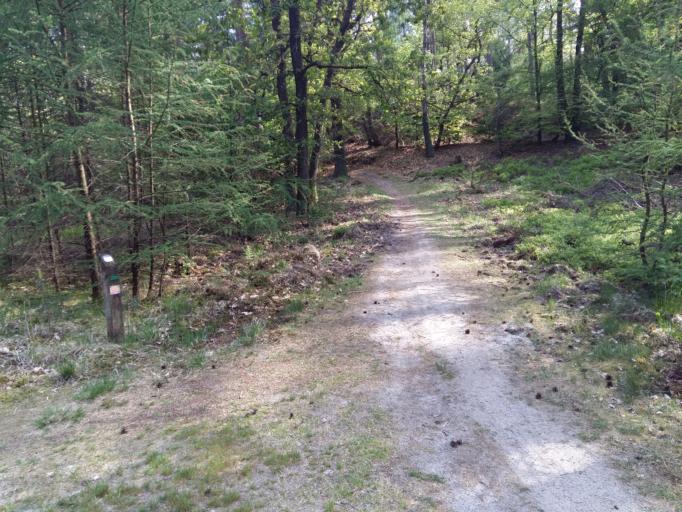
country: NL
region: Gelderland
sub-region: Gemeente Nunspeet
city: Nunspeet
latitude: 52.3240
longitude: 5.7164
